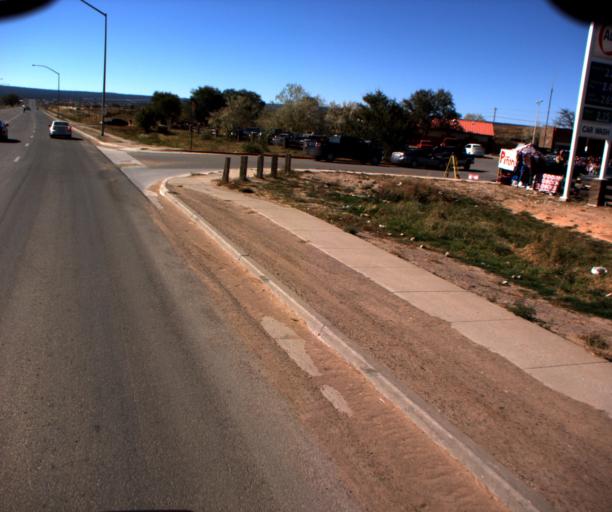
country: US
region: Arizona
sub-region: Apache County
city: Window Rock
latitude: 35.6634
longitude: -109.0579
